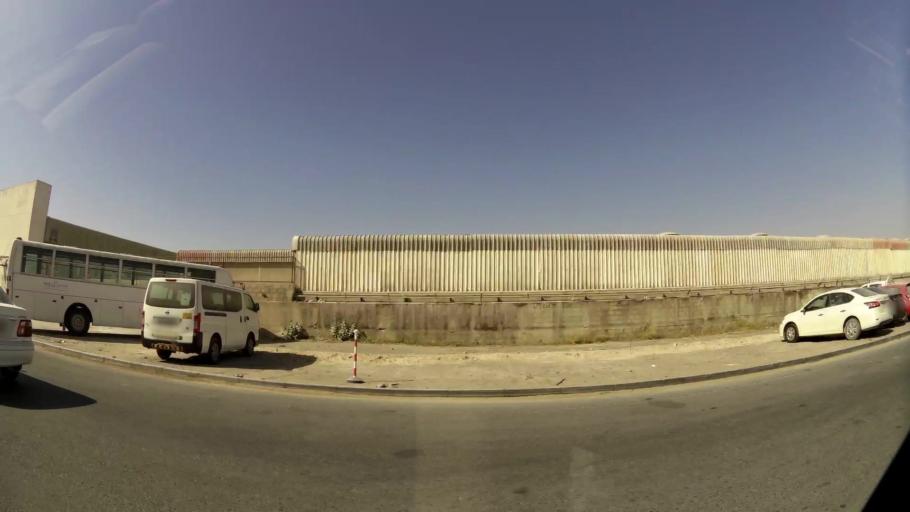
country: AE
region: Dubai
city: Dubai
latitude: 25.1266
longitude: 55.2192
